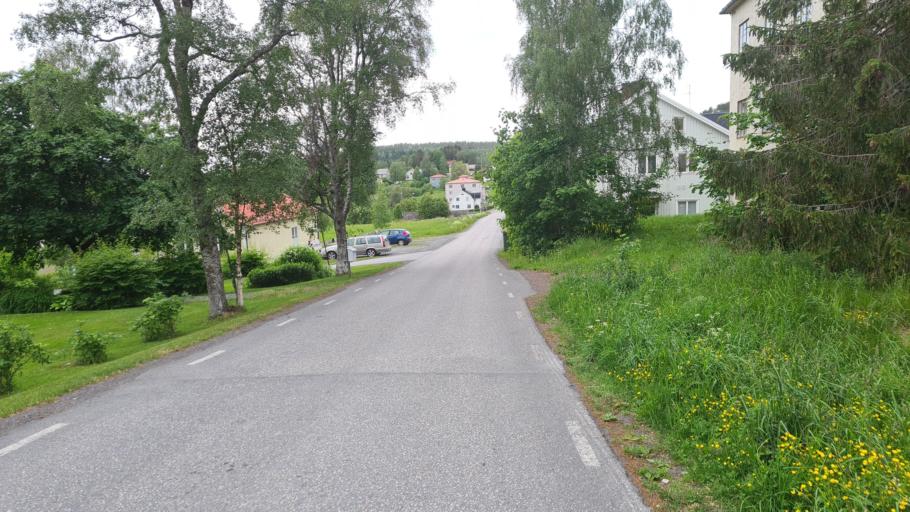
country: SE
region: Vaesternorrland
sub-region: Kramfors Kommun
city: Nordingra
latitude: 62.9837
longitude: 18.4322
